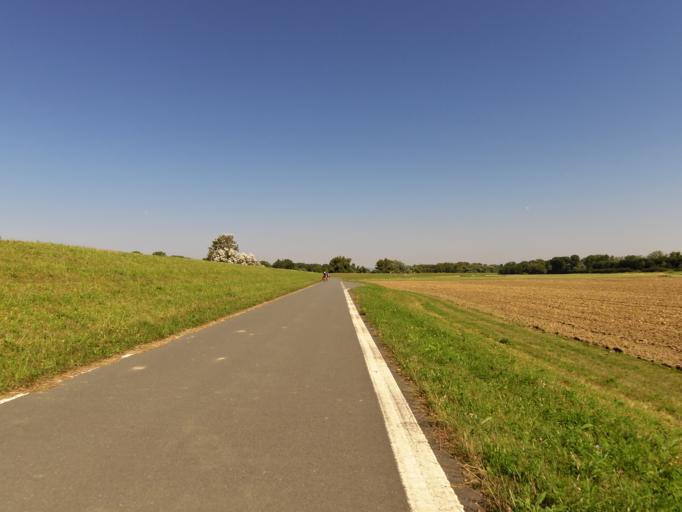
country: DE
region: Rheinland-Pfalz
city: Nackenheim
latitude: 49.9369
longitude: 8.3579
